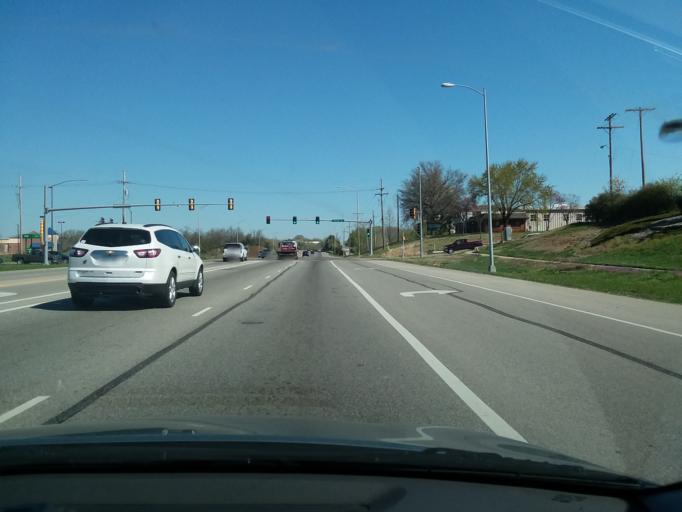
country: US
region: Kansas
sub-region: Johnson County
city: Olathe
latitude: 38.8866
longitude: -94.8345
